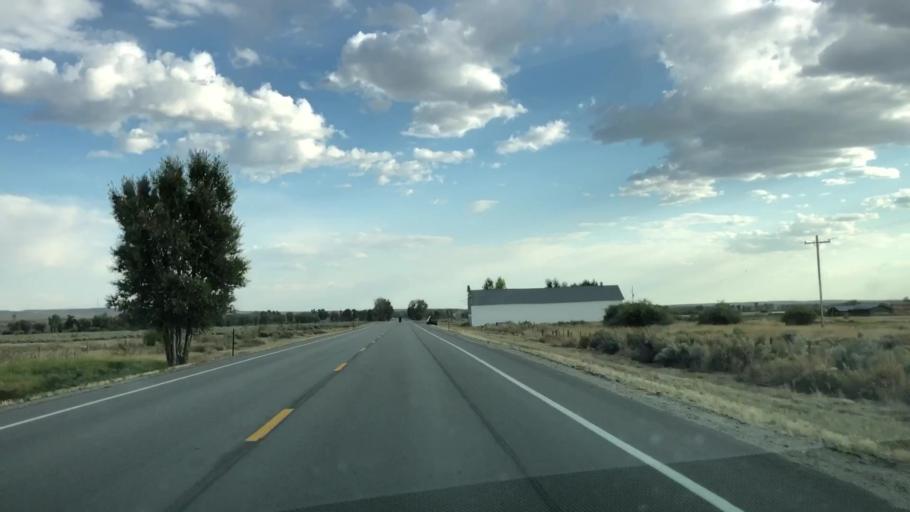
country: US
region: Wyoming
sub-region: Sublette County
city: Pinedale
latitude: 42.7043
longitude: -109.7135
